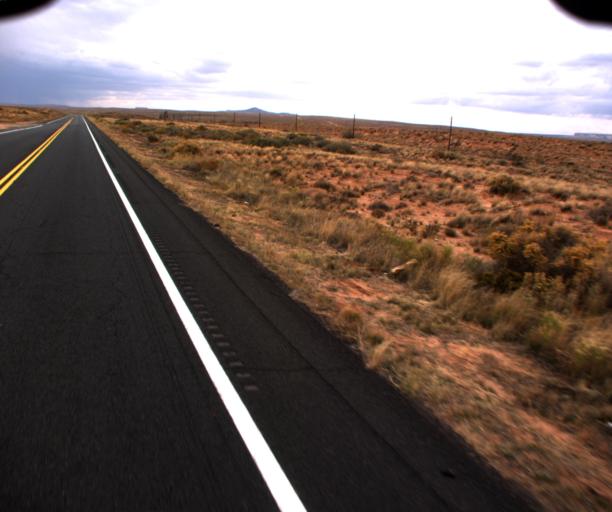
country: US
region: Arizona
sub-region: Coconino County
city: Kaibito
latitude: 36.3979
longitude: -110.8627
